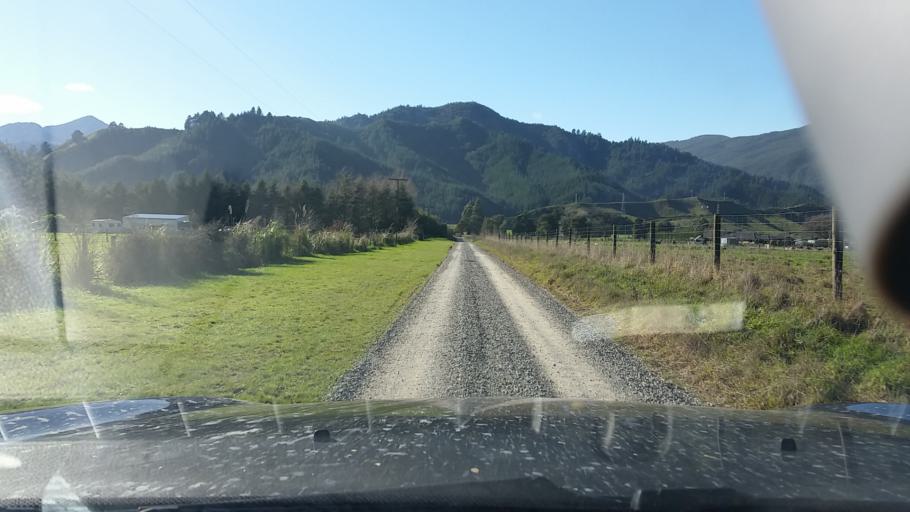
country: NZ
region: Marlborough
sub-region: Marlborough District
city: Blenheim
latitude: -41.4328
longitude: 173.7599
